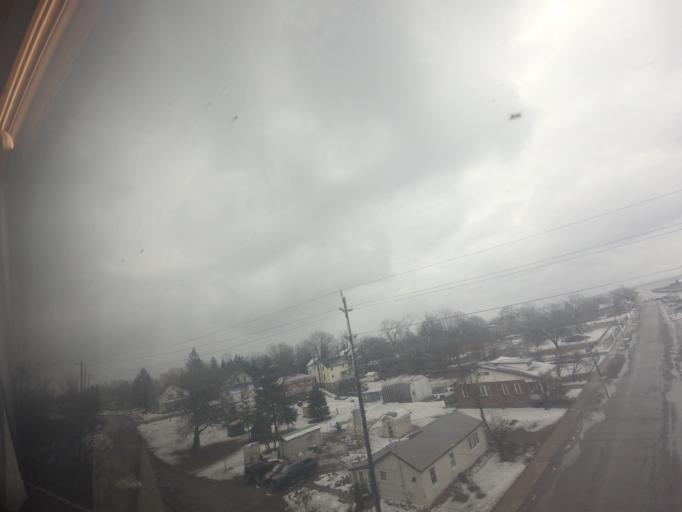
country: CA
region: Ontario
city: Cobourg
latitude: 43.9470
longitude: -78.2915
